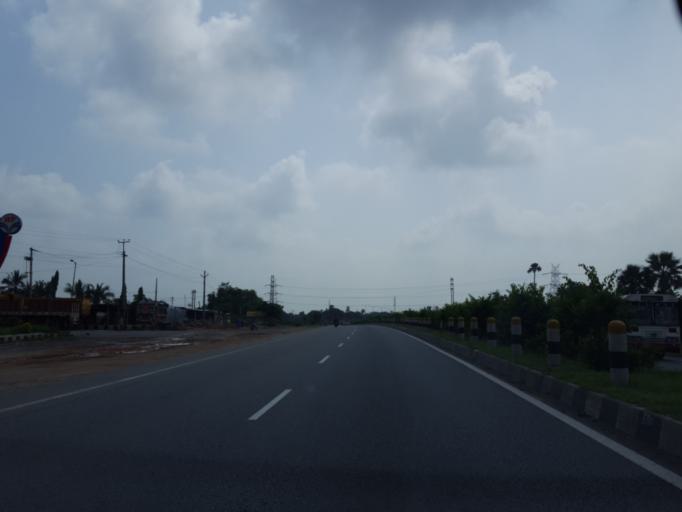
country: IN
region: Telangana
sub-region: Nalgonda
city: Gudur
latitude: 17.2646
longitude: 78.8338
